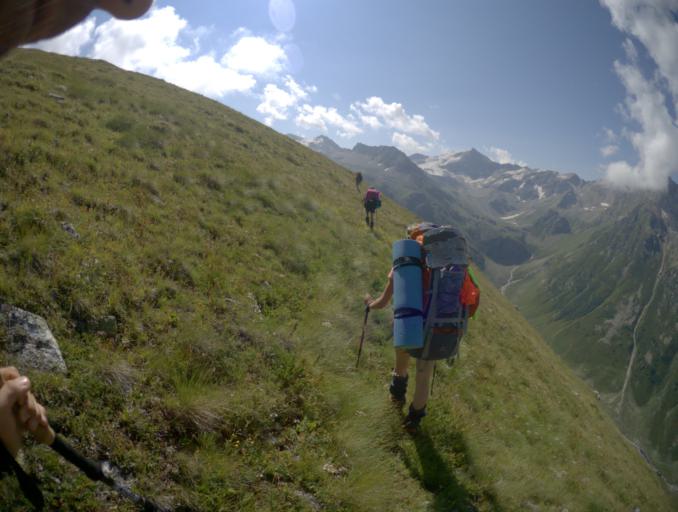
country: RU
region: Karachayevo-Cherkesiya
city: Uchkulan
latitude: 43.3019
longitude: 42.0604
